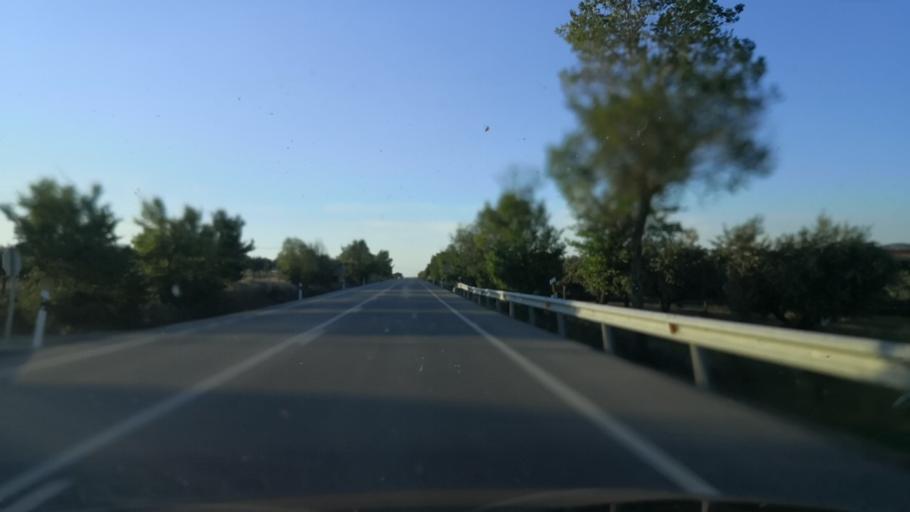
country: ES
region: Extremadura
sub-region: Provincia de Caceres
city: Valencia de Alcantara
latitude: 39.4356
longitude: -7.2236
